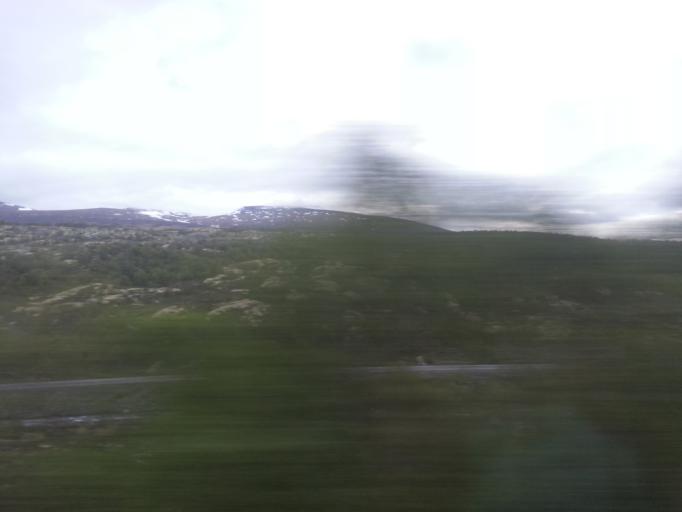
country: NO
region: Sor-Trondelag
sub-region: Oppdal
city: Oppdal
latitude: 62.2869
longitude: 9.5958
